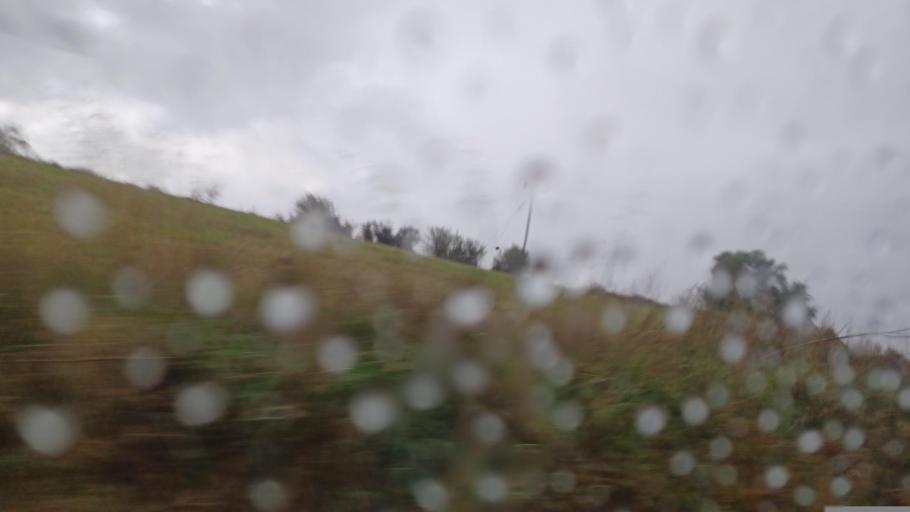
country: CY
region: Pafos
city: Mesogi
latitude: 34.8650
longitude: 32.5454
